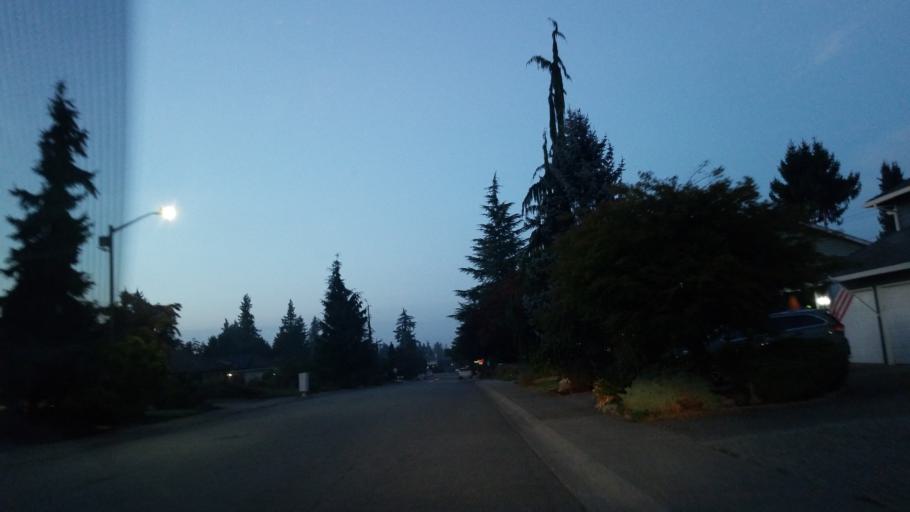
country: US
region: Washington
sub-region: Snohomish County
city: Silver Firs
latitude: 47.8855
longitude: -122.1715
